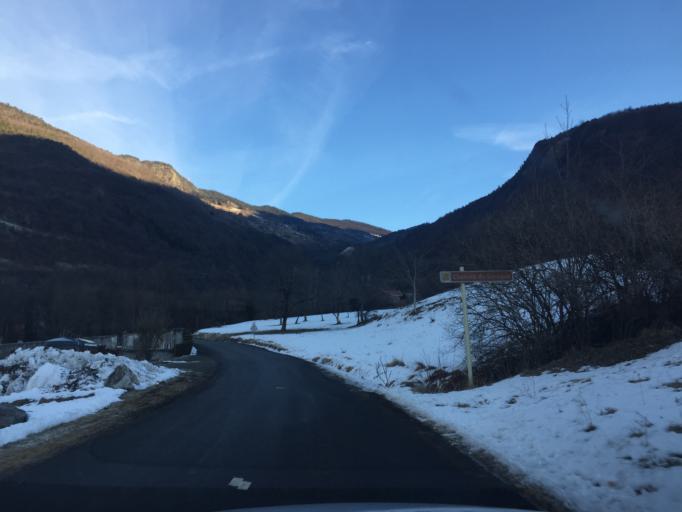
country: FR
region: Rhone-Alpes
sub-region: Departement de la Savoie
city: Aigueblanche
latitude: 45.5212
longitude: 6.4916
